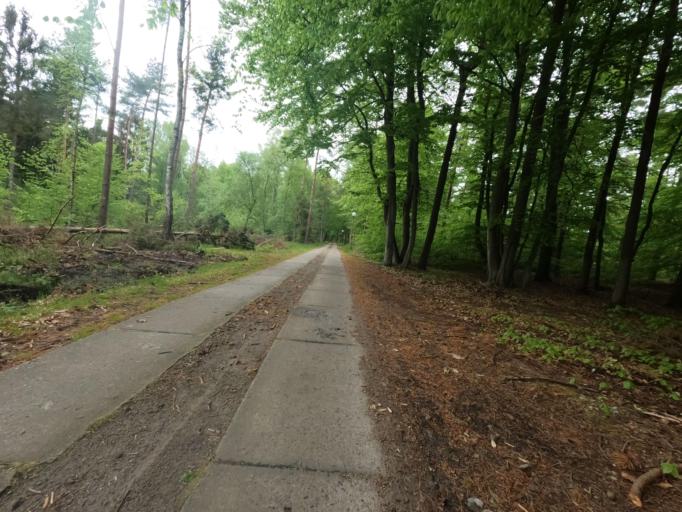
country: DE
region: Mecklenburg-Vorpommern
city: Born
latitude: 54.4019
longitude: 12.4914
